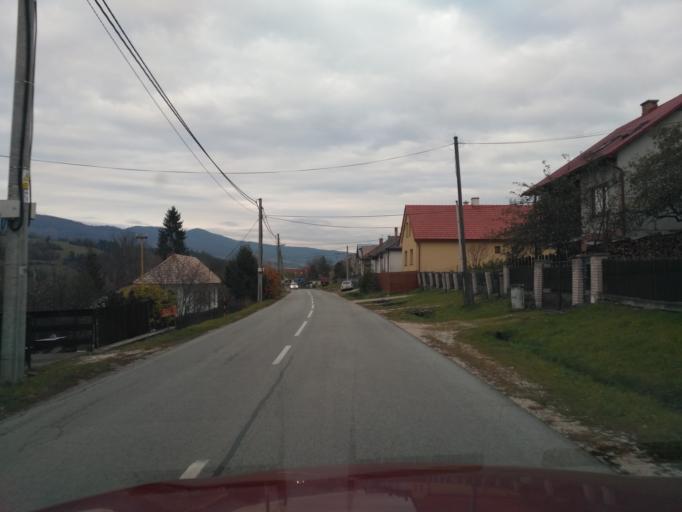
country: SK
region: Kosicky
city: Krompachy
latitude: 48.8006
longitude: 20.7933
